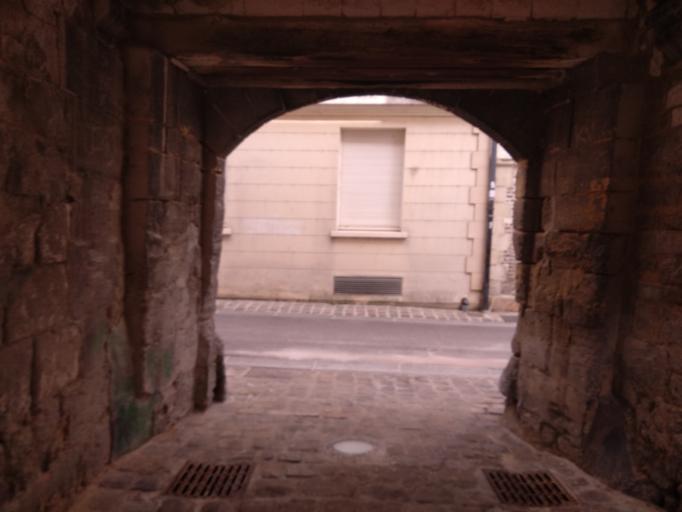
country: FR
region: Champagne-Ardenne
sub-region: Departement de la Marne
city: Chalons-en-Champagne
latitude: 48.9555
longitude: 4.3597
